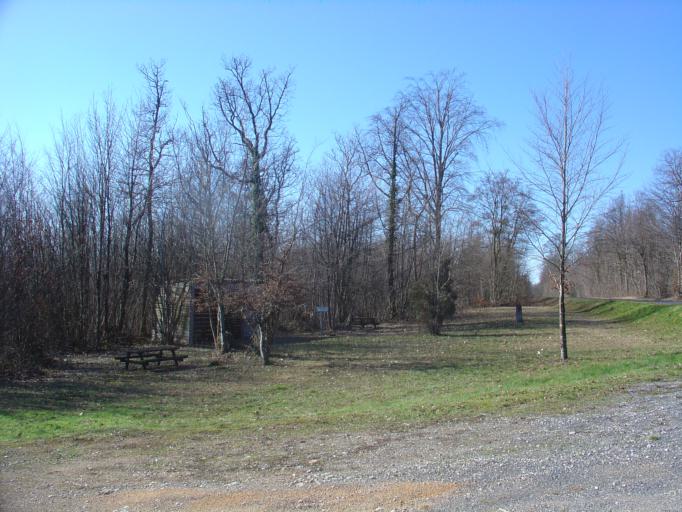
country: FR
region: Lorraine
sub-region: Departement de Meurthe-et-Moselle
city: Blenod-les-Toul
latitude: 48.5671
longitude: 5.8108
